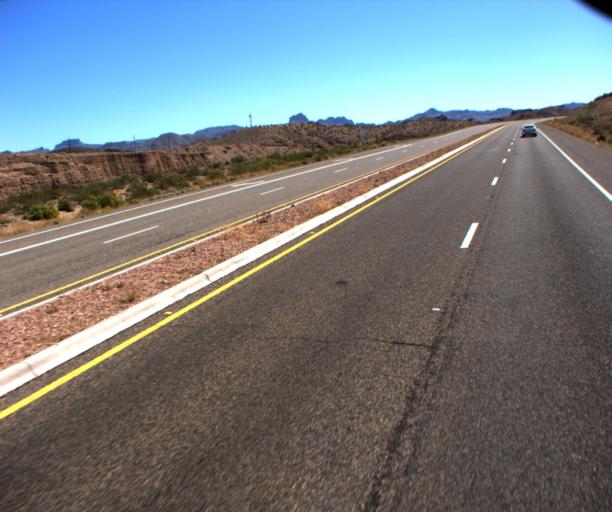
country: US
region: Nevada
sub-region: Clark County
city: Laughlin
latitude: 35.1909
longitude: -114.5216
